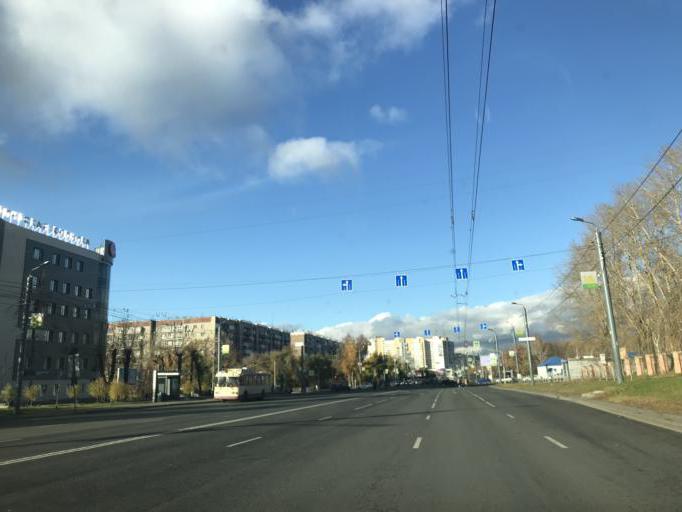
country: RU
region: Chelyabinsk
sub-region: Gorod Chelyabinsk
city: Chelyabinsk
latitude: 55.1656
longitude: 61.4525
